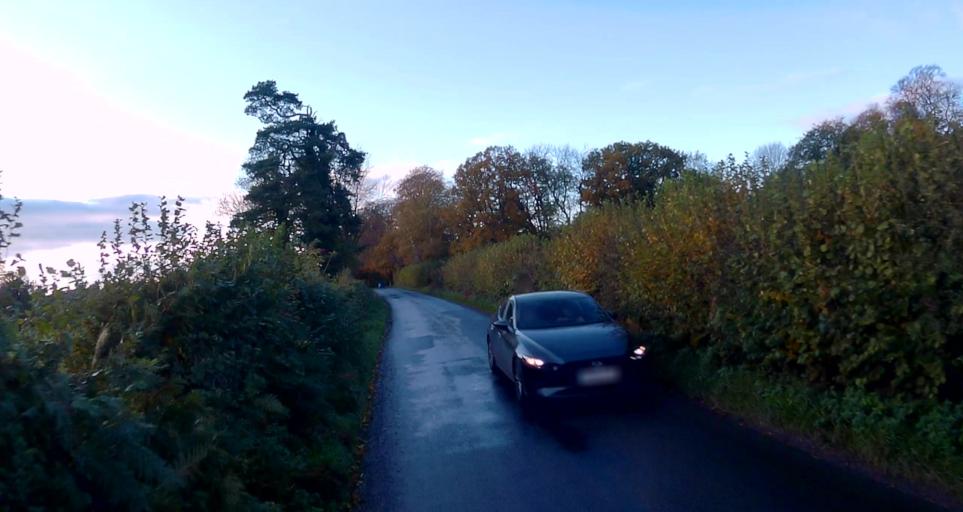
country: GB
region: England
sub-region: Hampshire
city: Basingstoke
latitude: 51.1857
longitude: -1.0743
